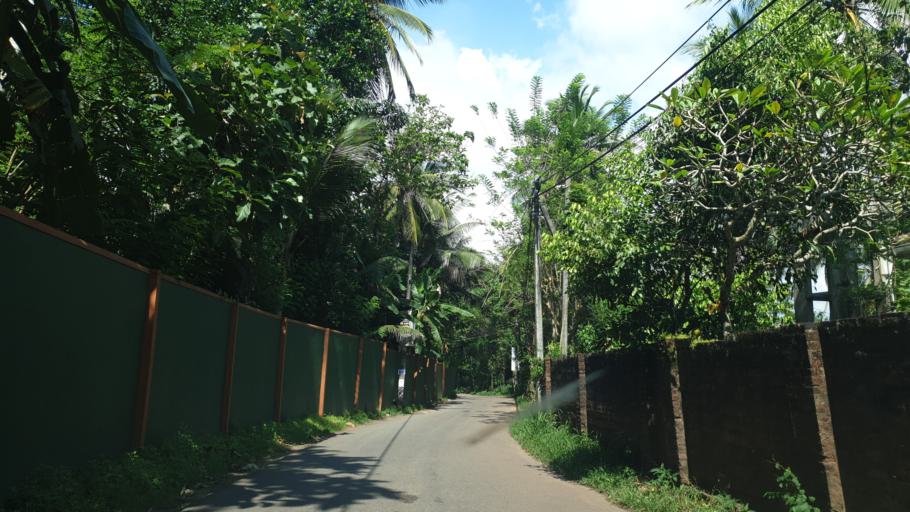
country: LK
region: Western
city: Panadura
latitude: 6.7080
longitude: 79.9582
